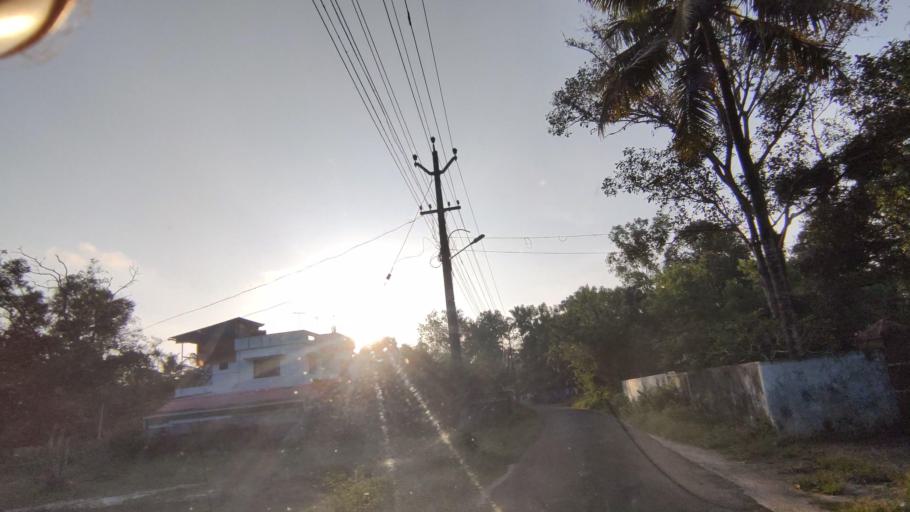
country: IN
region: Kerala
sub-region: Alappuzha
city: Shertallai
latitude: 9.6471
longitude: 76.3390
